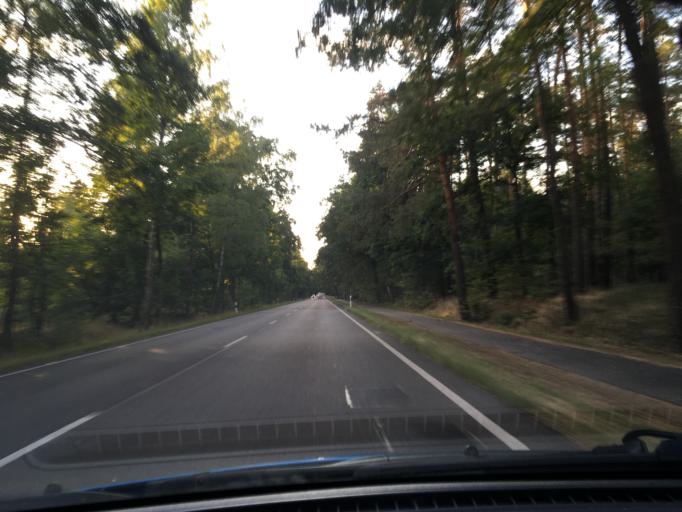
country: DE
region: Lower Saxony
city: Celle
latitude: 52.6623
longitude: 10.0473
